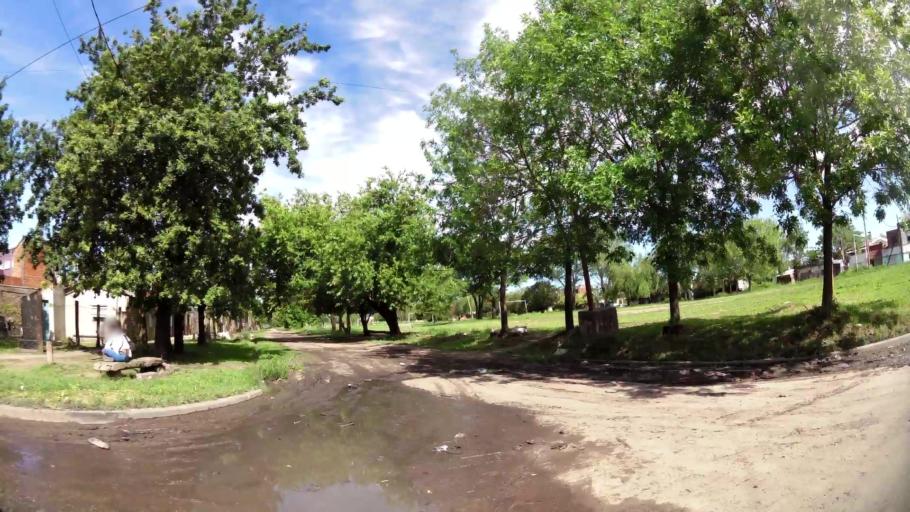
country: AR
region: Buenos Aires
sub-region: Partido de Almirante Brown
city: Adrogue
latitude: -34.7846
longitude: -58.3108
